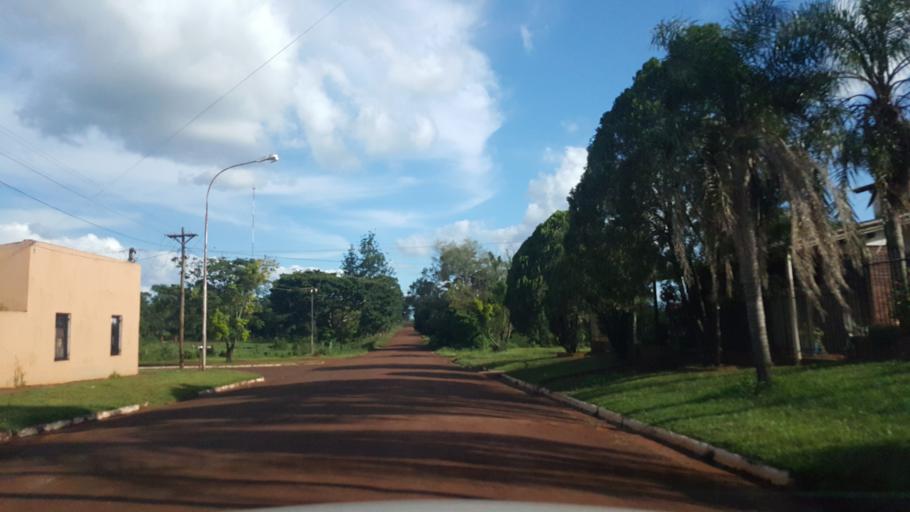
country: AR
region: Misiones
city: Santa Ana
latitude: -27.3706
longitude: -55.5853
